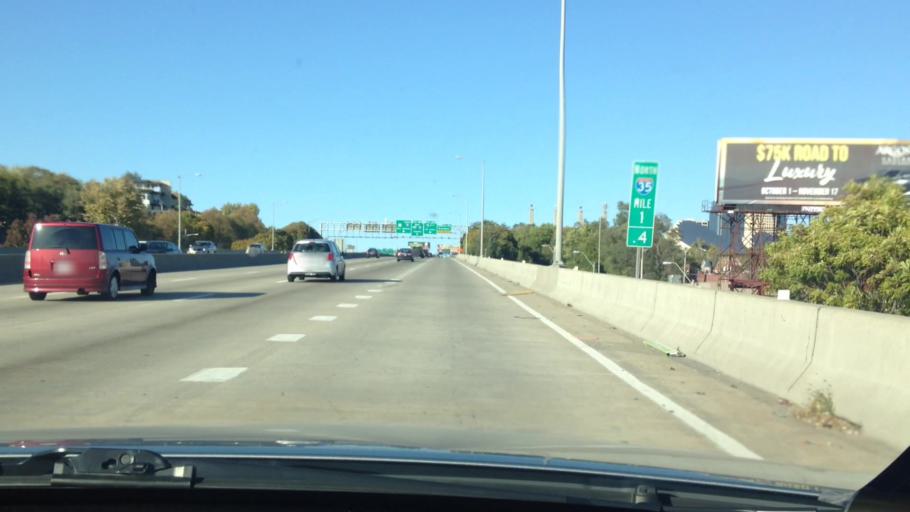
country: US
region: Missouri
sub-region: Jackson County
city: Kansas City
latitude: 39.0879
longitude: -94.5916
